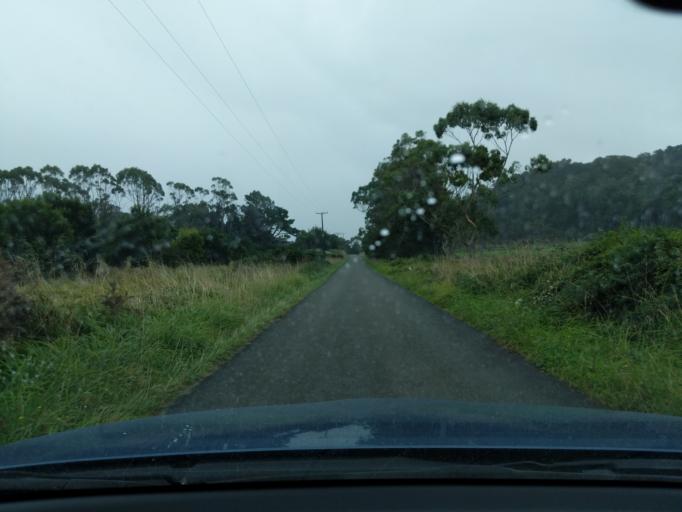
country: NZ
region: Tasman
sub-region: Tasman District
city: Takaka
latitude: -40.6374
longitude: 172.4884
